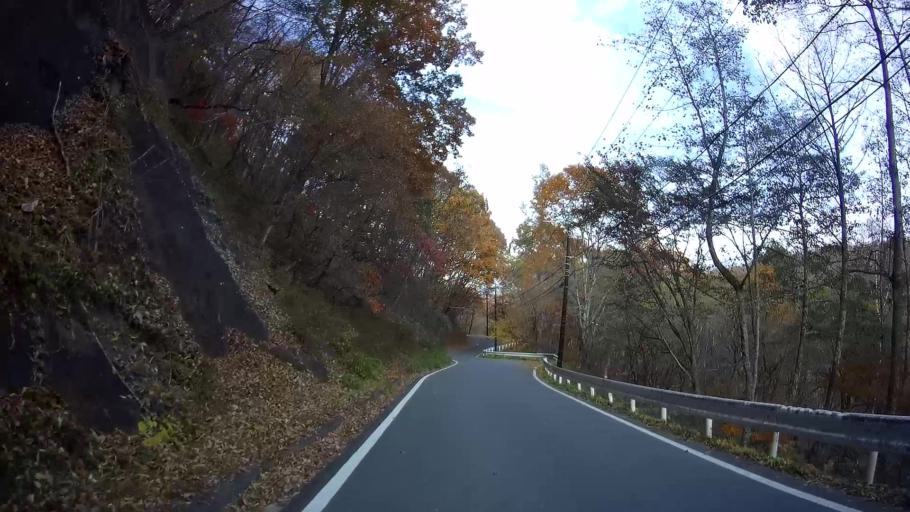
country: JP
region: Gunma
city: Nakanojomachi
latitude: 36.6612
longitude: 138.6660
